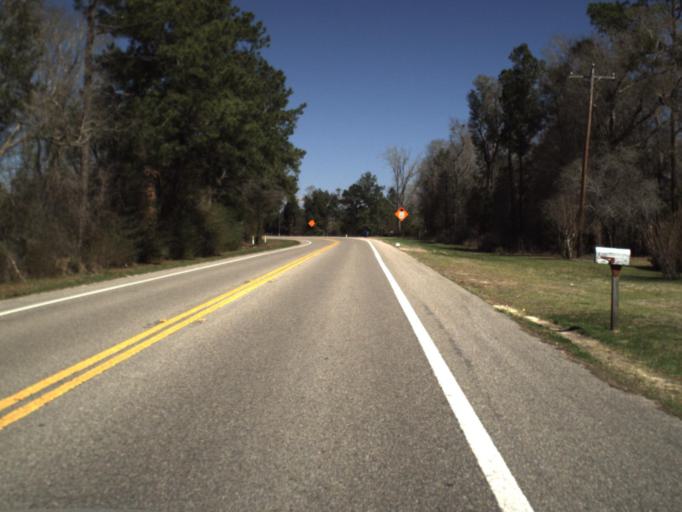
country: US
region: Florida
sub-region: Calhoun County
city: Blountstown
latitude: 30.4875
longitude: -85.0450
